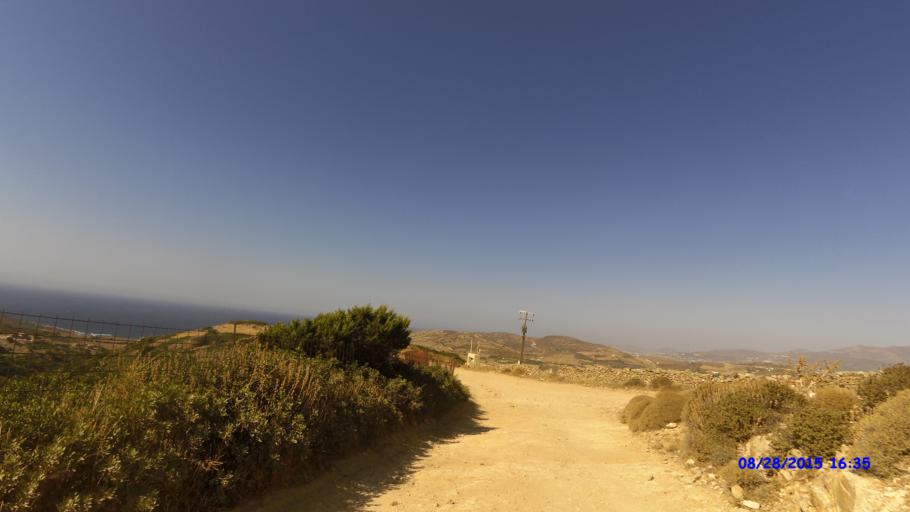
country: GR
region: South Aegean
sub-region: Nomos Kykladon
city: Antiparos
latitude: 37.0069
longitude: 25.0452
